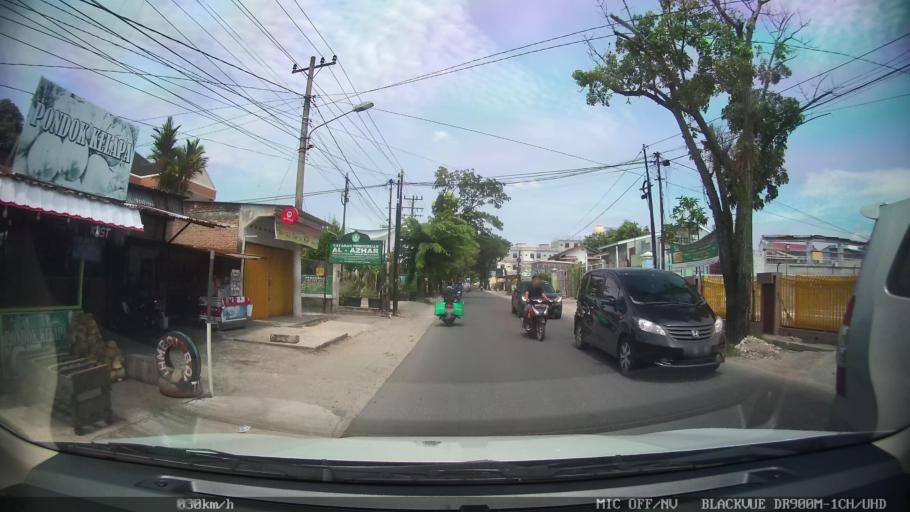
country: ID
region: North Sumatra
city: Sunggal
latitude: 3.5847
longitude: 98.6287
